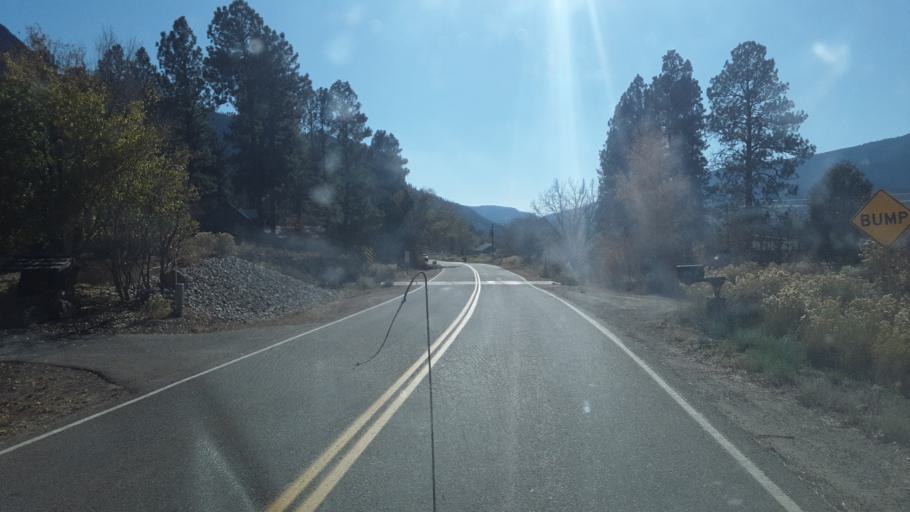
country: US
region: Colorado
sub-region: La Plata County
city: Durango
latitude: 37.4104
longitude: -107.8126
